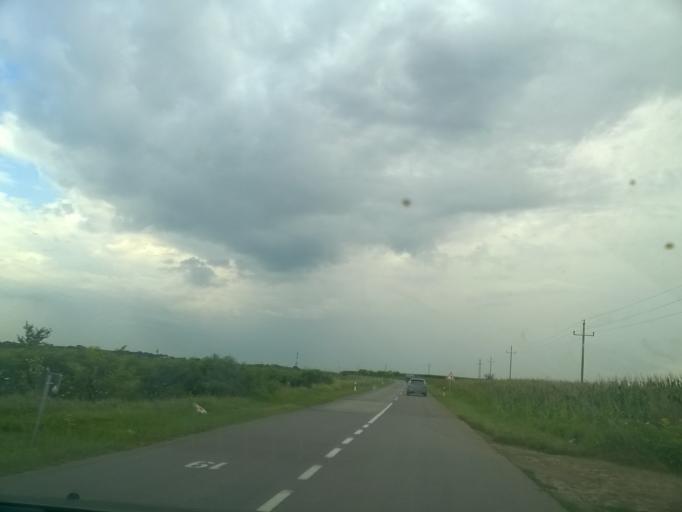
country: RS
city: Tomasevac
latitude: 45.2512
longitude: 20.6298
